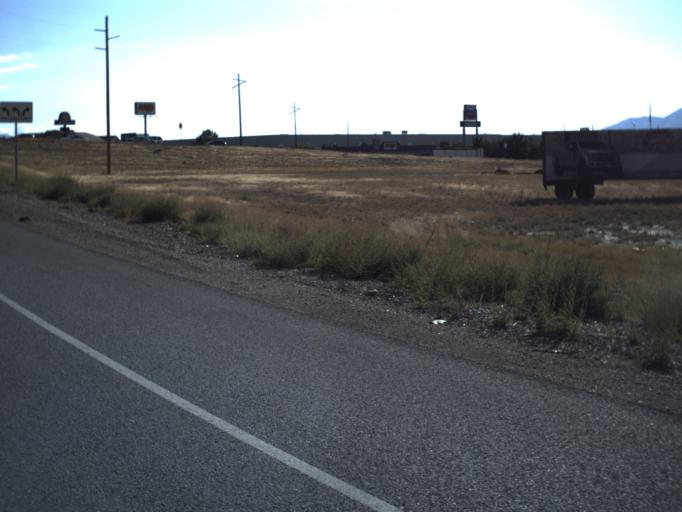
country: US
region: Utah
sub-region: Utah County
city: Springville
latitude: 40.1632
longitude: -111.6471
